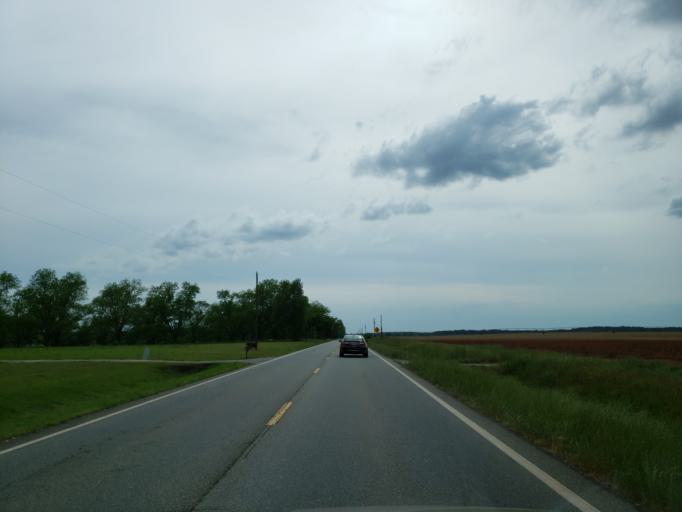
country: US
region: Georgia
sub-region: Houston County
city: Perry
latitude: 32.4312
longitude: -83.8138
